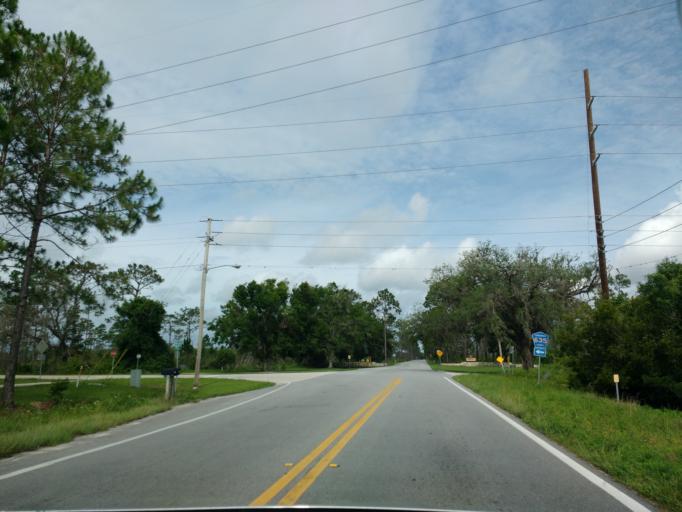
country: US
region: Florida
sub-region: Highlands County
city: Sebring
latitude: 27.4709
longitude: -81.5143
